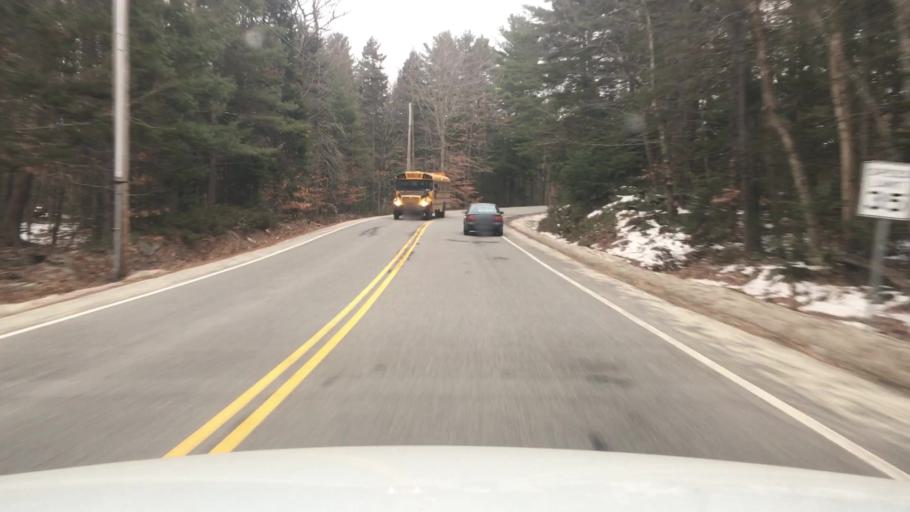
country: US
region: Maine
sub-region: Cumberland County
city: Freeport
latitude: 43.8768
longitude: -70.0514
